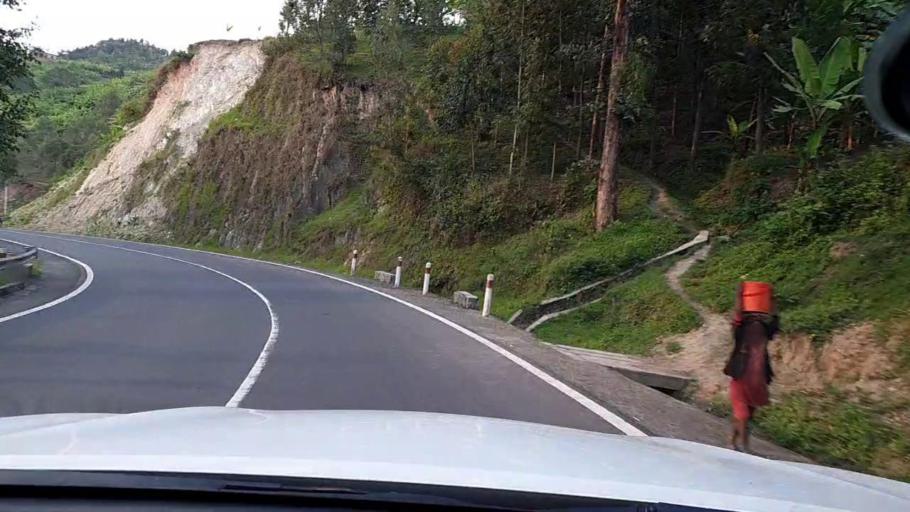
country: RW
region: Western Province
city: Kibuye
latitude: -2.0843
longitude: 29.4093
